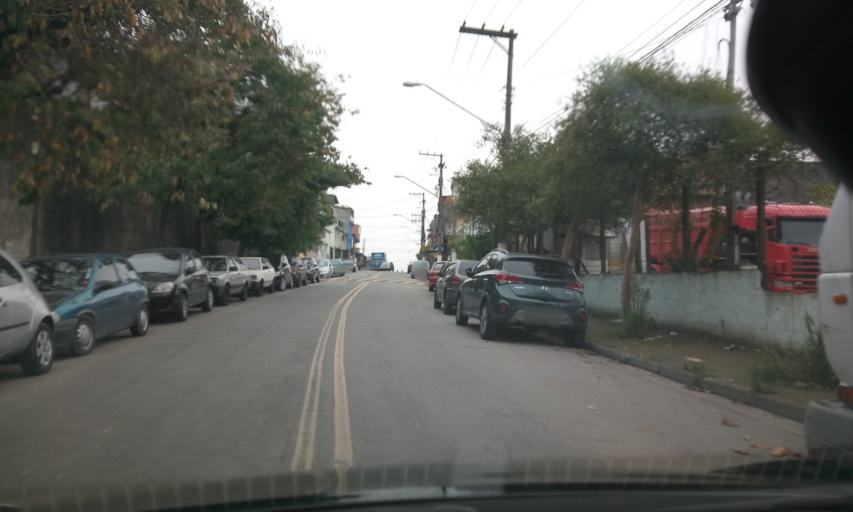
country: BR
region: Sao Paulo
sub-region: Sao Bernardo Do Campo
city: Sao Bernardo do Campo
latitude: -23.7048
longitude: -46.5623
